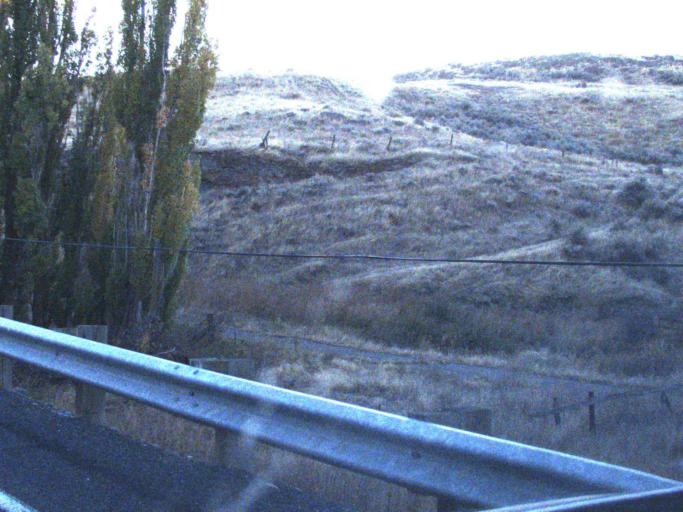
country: US
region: Washington
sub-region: Franklin County
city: Connell
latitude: 46.6551
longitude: -118.4972
